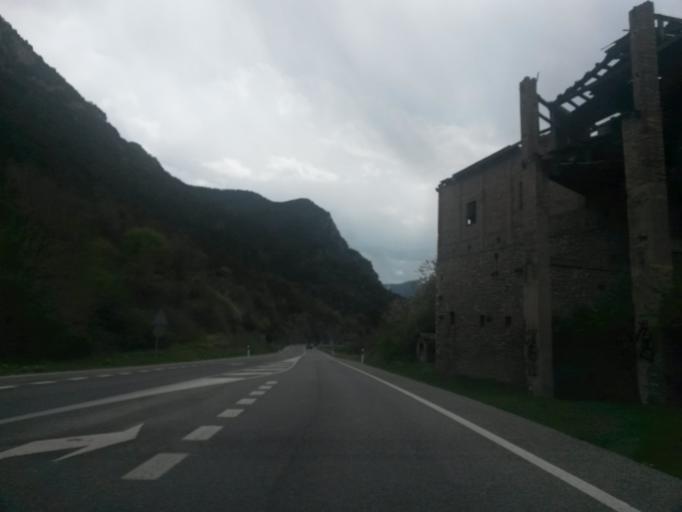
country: ES
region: Catalonia
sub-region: Provincia de Barcelona
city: Sant Julia de Cerdanyola
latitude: 42.1932
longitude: 1.8692
